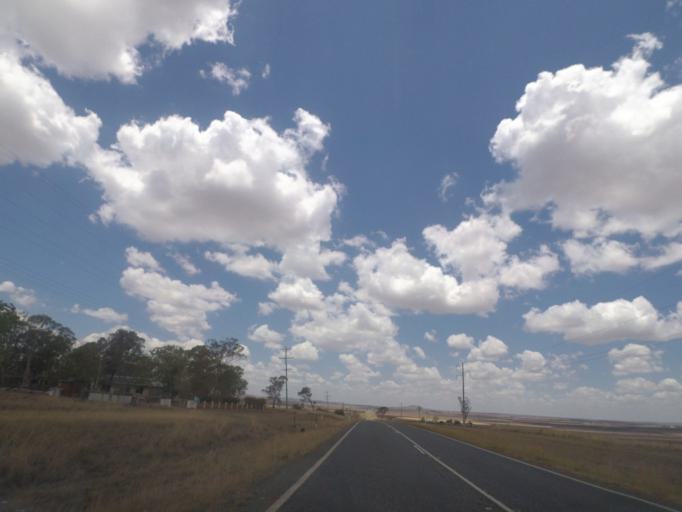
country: AU
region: Queensland
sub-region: Toowoomba
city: Top Camp
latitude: -27.8851
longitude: 151.9712
